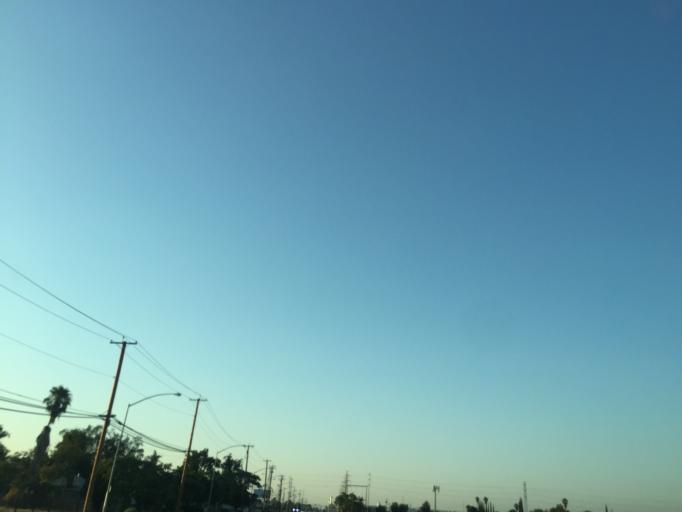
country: US
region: California
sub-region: Fresno County
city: Sunnyside
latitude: 36.7450
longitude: -119.7000
